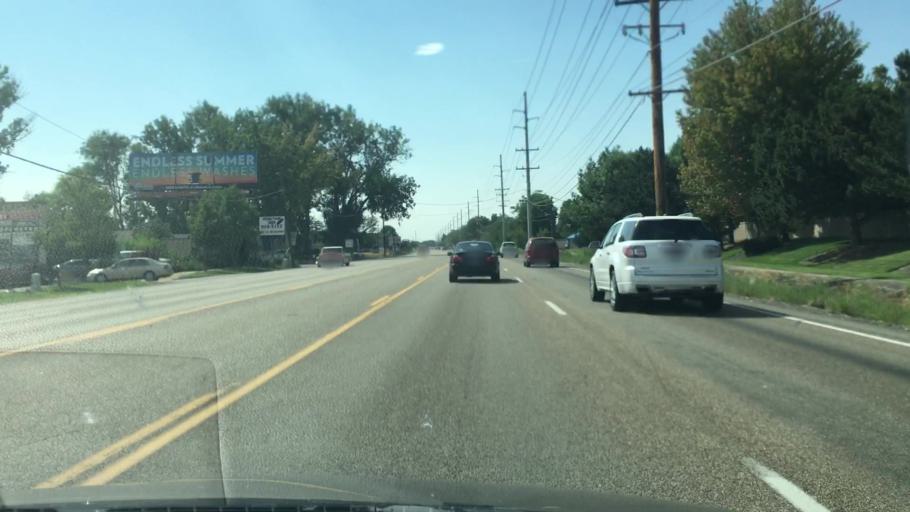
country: US
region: Idaho
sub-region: Ada County
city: Eagle
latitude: 43.6776
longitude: -116.2997
